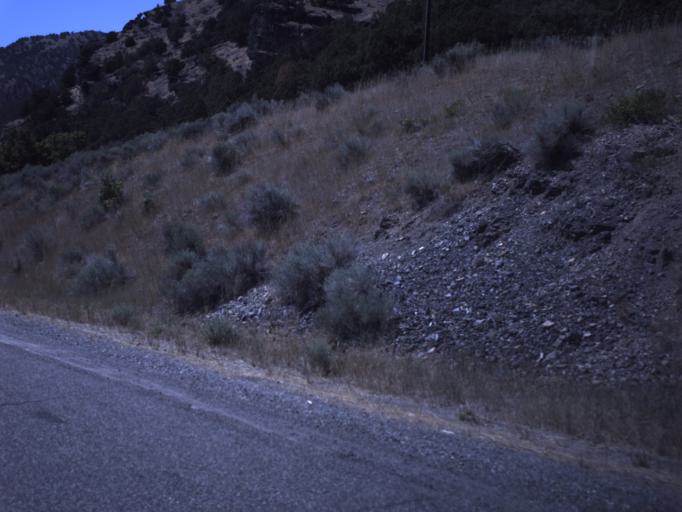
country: US
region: Utah
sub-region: Cache County
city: North Logan
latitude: 41.7483
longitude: -111.7370
